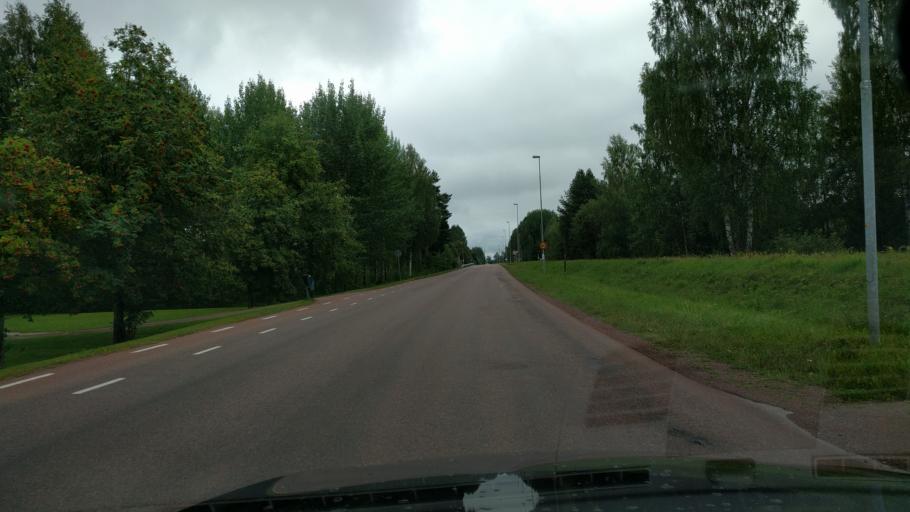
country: SE
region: Dalarna
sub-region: Mora Kommun
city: Mora
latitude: 61.0065
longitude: 14.5198
